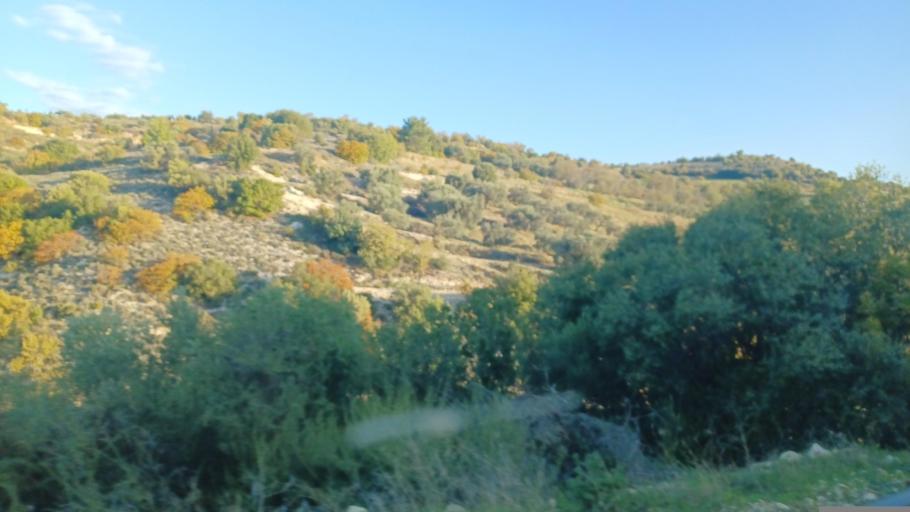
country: CY
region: Pafos
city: Mesogi
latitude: 34.8683
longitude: 32.5782
